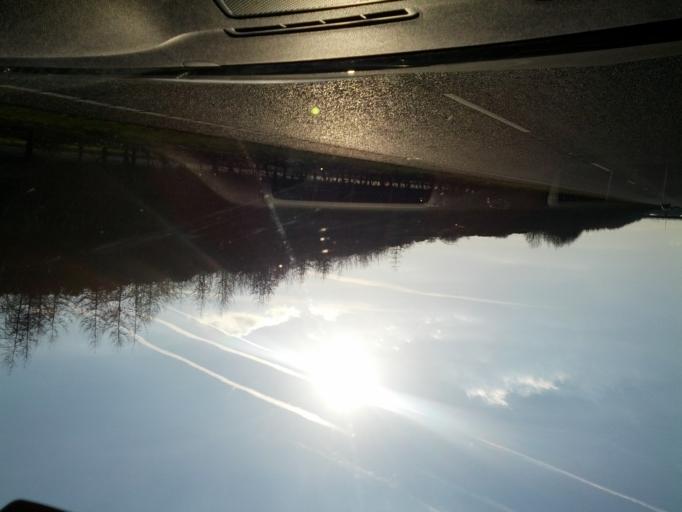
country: IE
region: Leinster
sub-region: Laois
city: Stradbally
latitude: 53.0650
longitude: -7.2195
